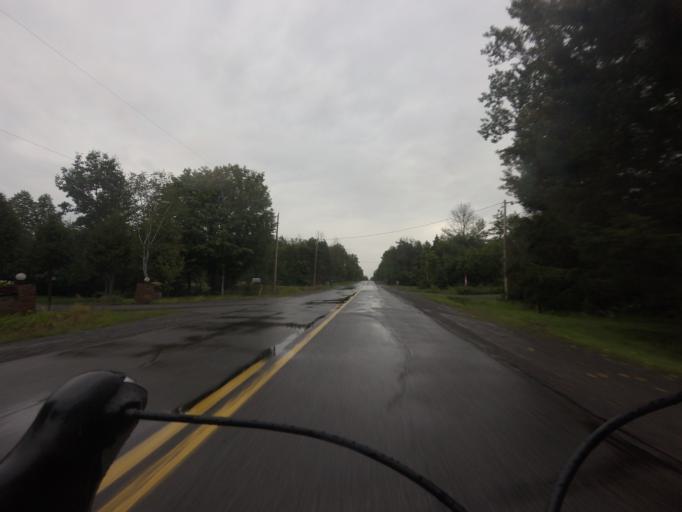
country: CA
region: Ontario
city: Bells Corners
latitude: 45.1961
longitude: -75.7177
